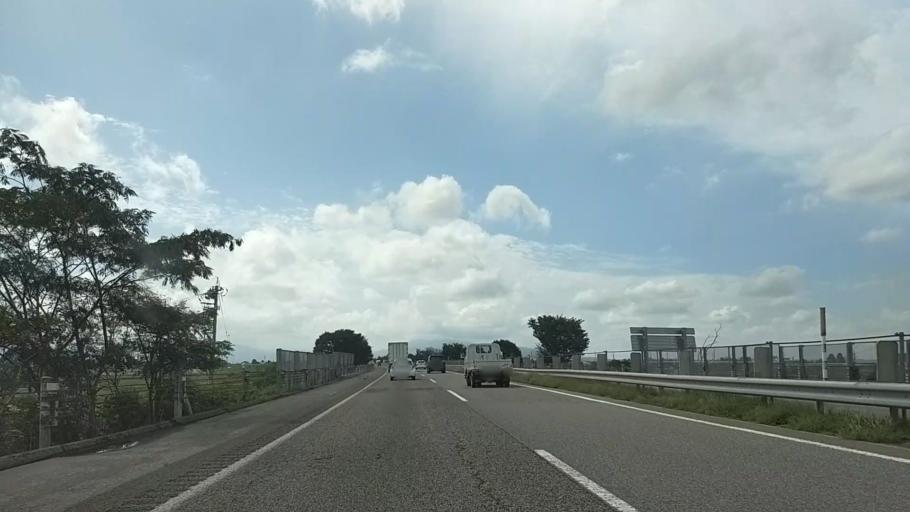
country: JP
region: Toyama
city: Nanto-shi
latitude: 36.6469
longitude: 136.9815
